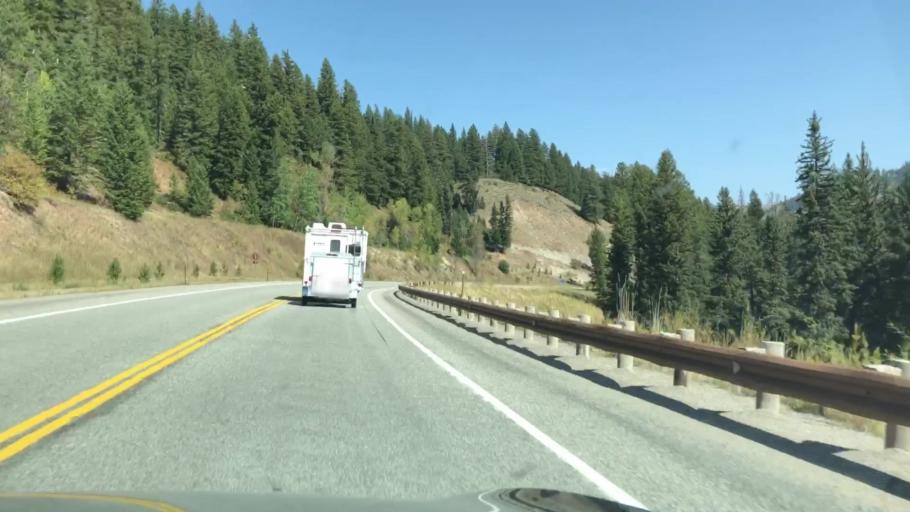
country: US
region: Wyoming
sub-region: Teton County
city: Hoback
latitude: 43.2360
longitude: -110.7796
